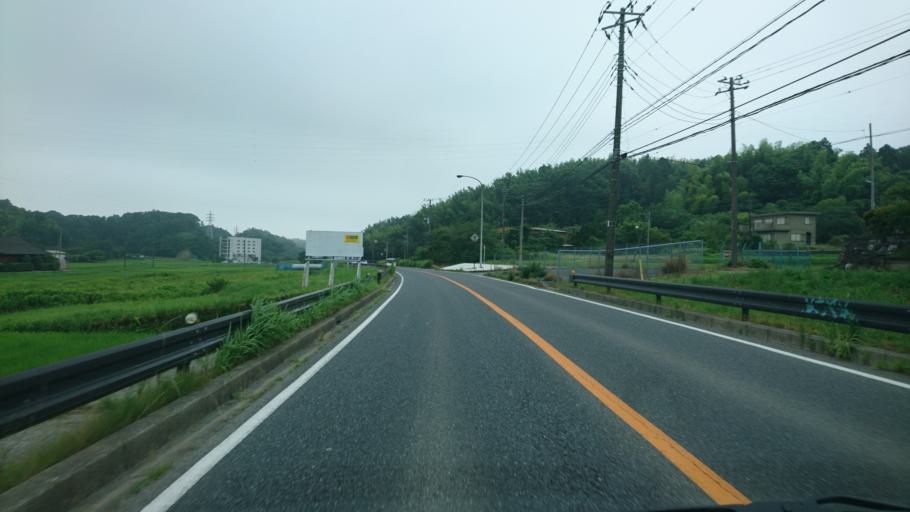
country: JP
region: Chiba
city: Kimitsu
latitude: 35.2705
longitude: 139.8966
